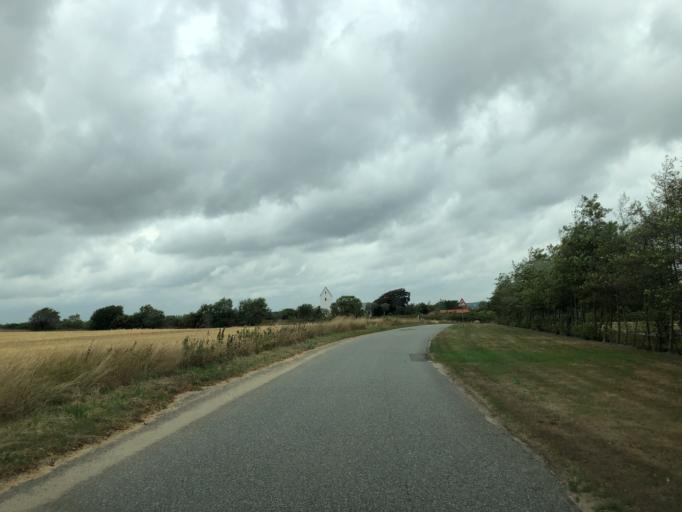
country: DK
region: Central Jutland
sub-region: Ringkobing-Skjern Kommune
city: Videbaek
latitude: 56.1096
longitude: 8.4994
